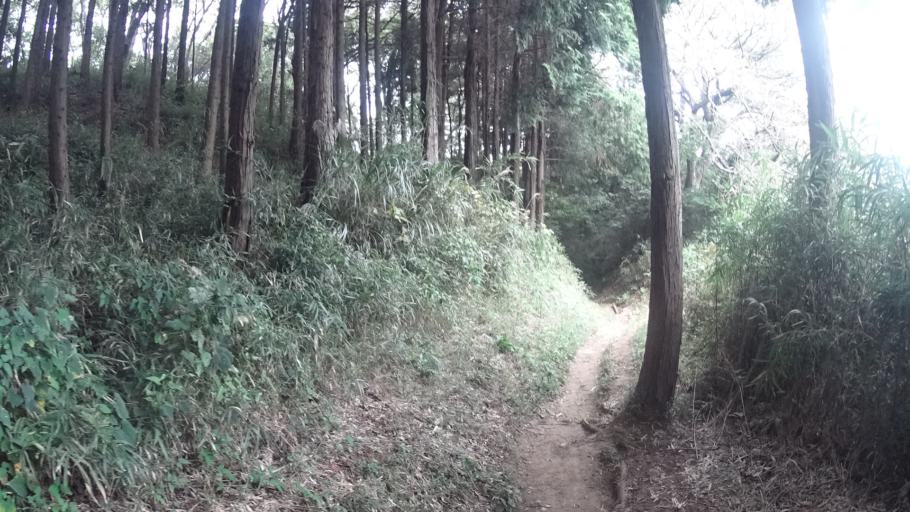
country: JP
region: Kanagawa
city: Zushi
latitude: 35.2943
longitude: 139.6018
